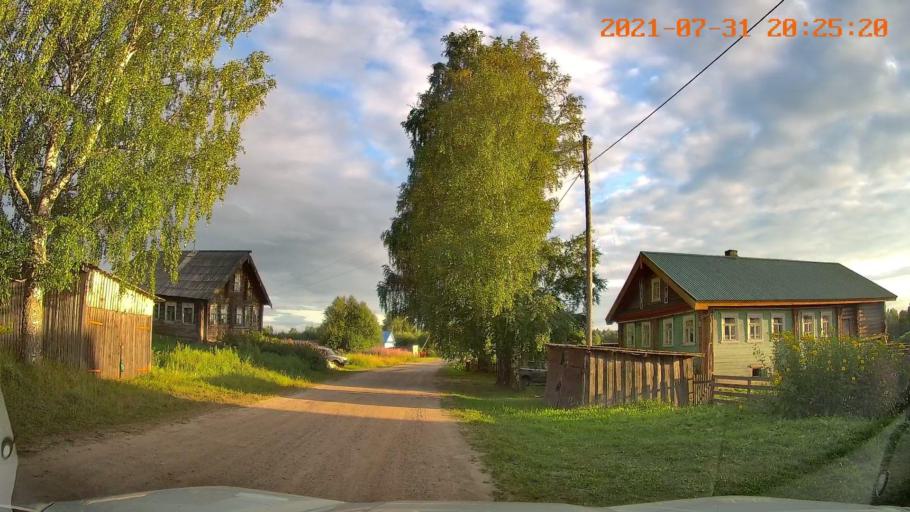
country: RU
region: Republic of Karelia
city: Pudozh
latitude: 61.6750
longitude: 36.3086
